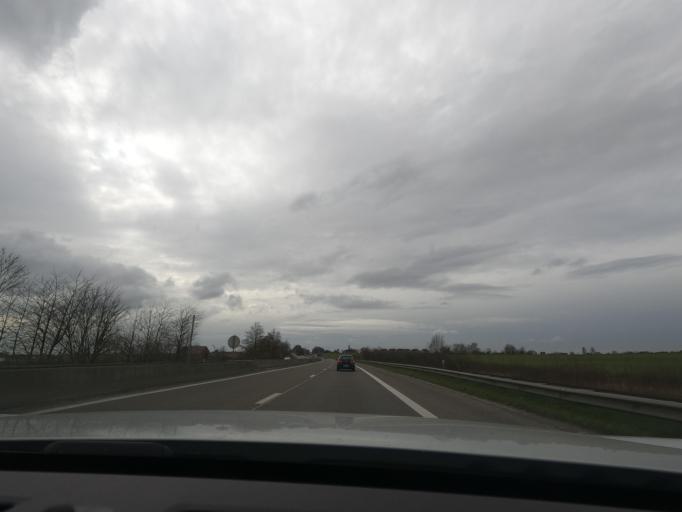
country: BE
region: Wallonia
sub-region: Province du Hainaut
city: Silly
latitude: 50.6889
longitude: 3.9377
